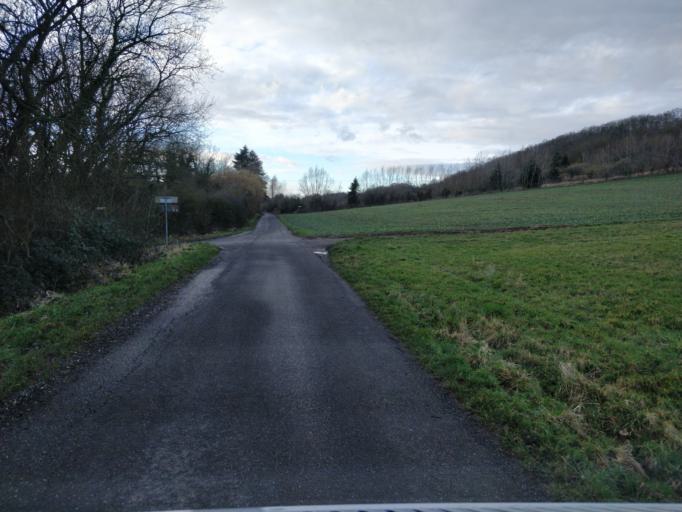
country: DE
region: Rheinland-Pfalz
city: Leutesdorf
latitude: 50.4578
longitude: 7.3920
